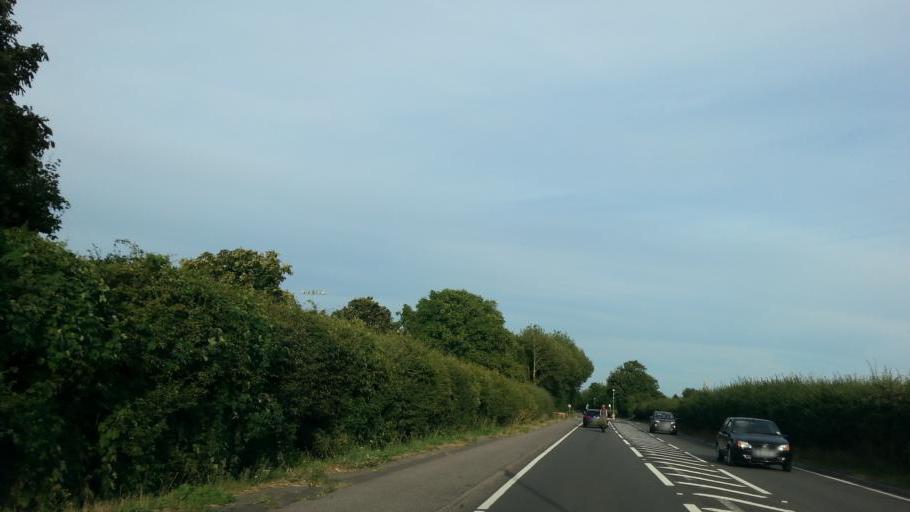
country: GB
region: England
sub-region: Nottinghamshire
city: Newark on Trent
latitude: 53.0830
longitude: -0.8291
